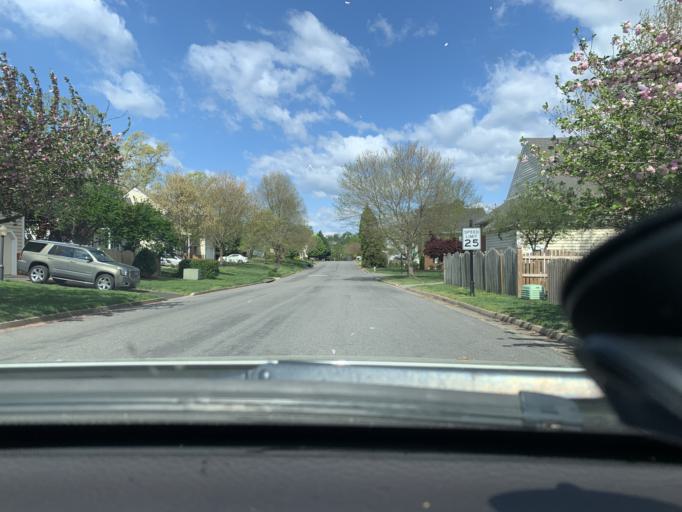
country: US
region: Virginia
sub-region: Henrico County
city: Tuckahoe
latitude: 37.5916
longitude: -77.5999
